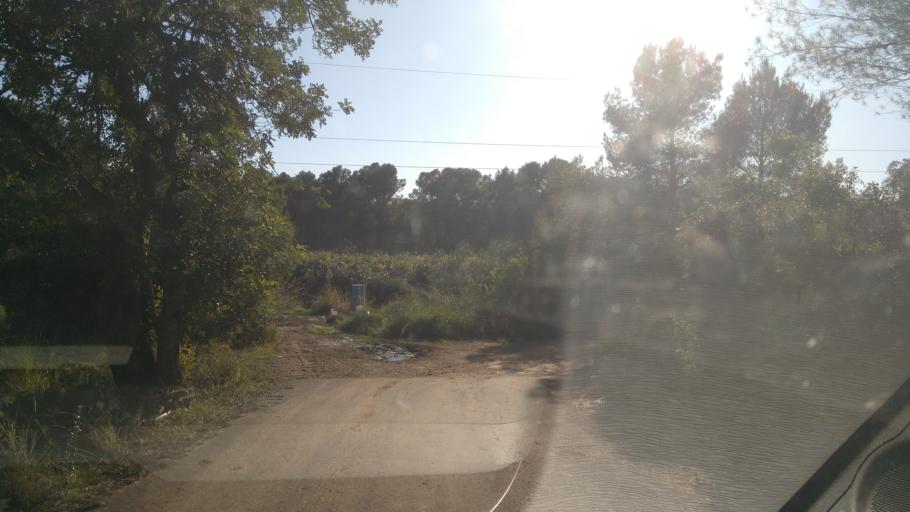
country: ES
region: Valencia
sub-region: Provincia de Valencia
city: Tous
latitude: 39.1746
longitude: -0.5603
